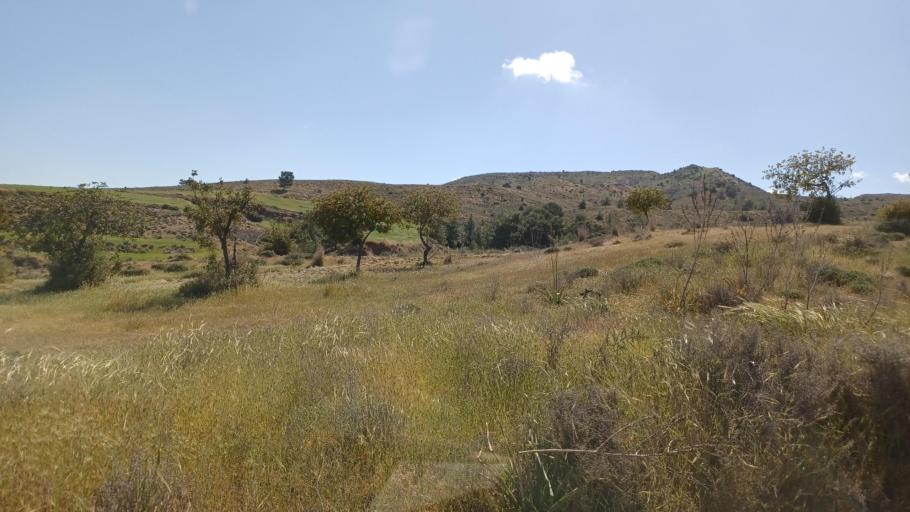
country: CY
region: Lefkosia
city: Peristerona
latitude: 35.0671
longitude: 33.0590
